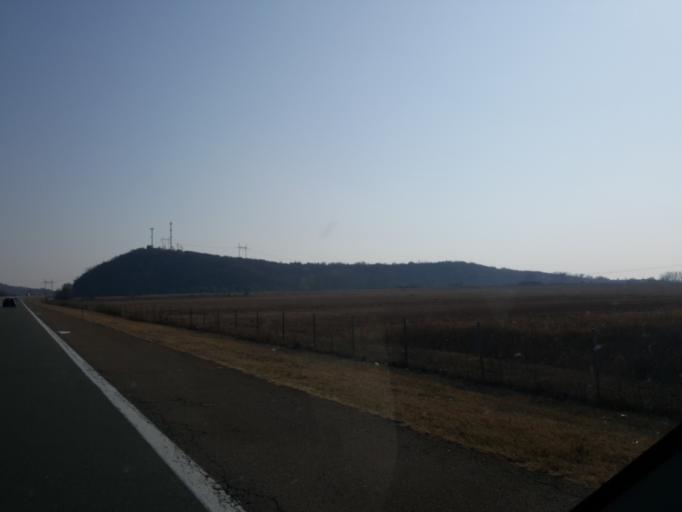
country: RS
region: Central Serbia
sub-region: Nisavski Okrug
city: Doljevac
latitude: 43.2295
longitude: 21.8273
